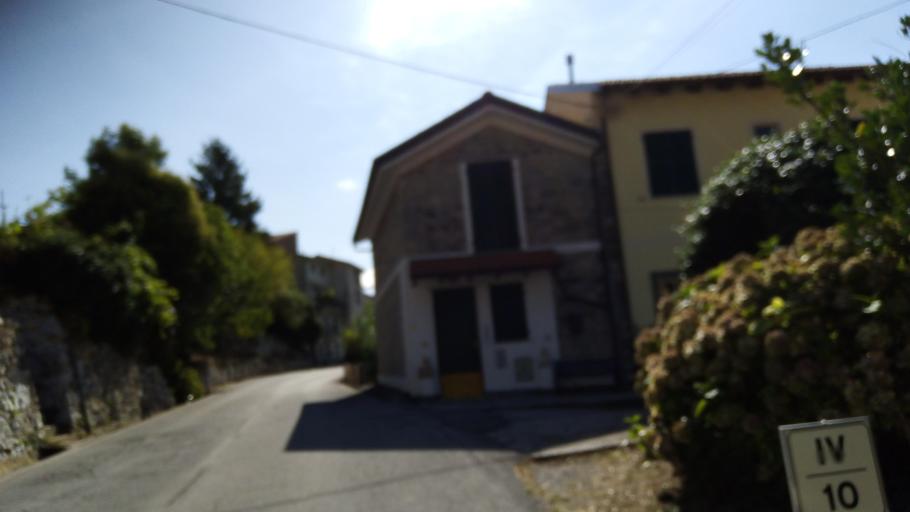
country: IT
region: Liguria
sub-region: Provincia di Savona
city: Balestrino
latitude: 44.1428
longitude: 8.1636
